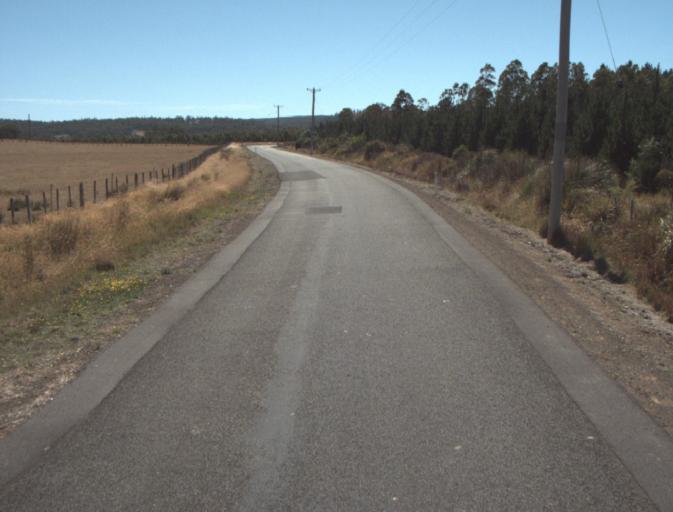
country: AU
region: Tasmania
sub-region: Launceston
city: Newstead
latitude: -41.3314
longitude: 147.3082
